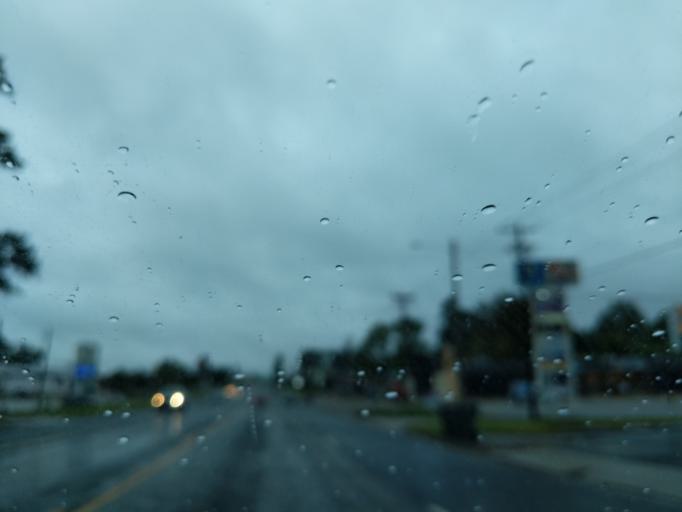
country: US
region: Texas
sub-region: Nacogdoches County
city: Nacogdoches
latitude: 31.6349
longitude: -94.6529
